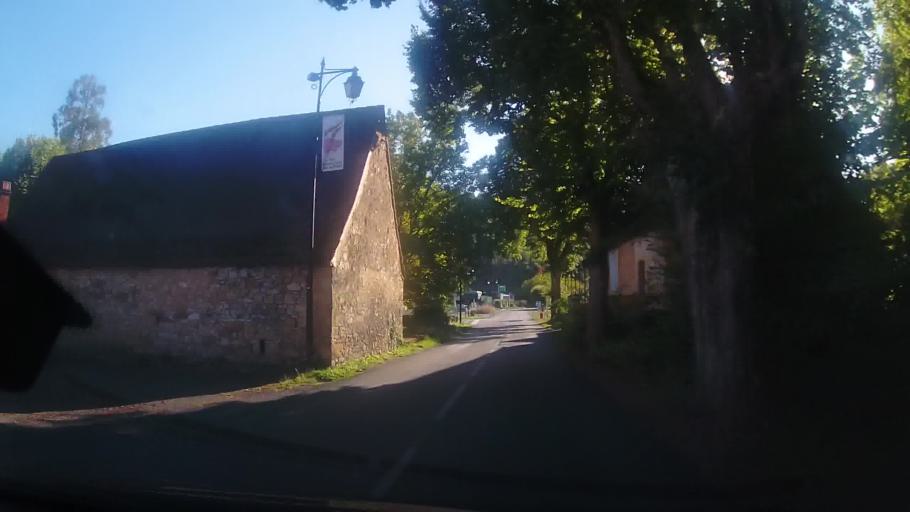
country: FR
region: Aquitaine
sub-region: Departement de la Dordogne
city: Cenac-et-Saint-Julien
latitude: 44.7892
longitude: 1.1699
